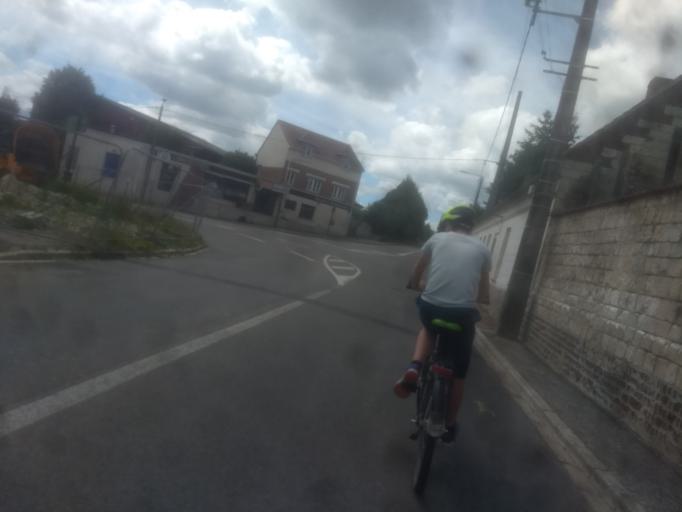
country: FR
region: Nord-Pas-de-Calais
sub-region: Departement du Pas-de-Calais
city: Mont-Saint-Eloi
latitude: 50.3476
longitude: 2.6527
